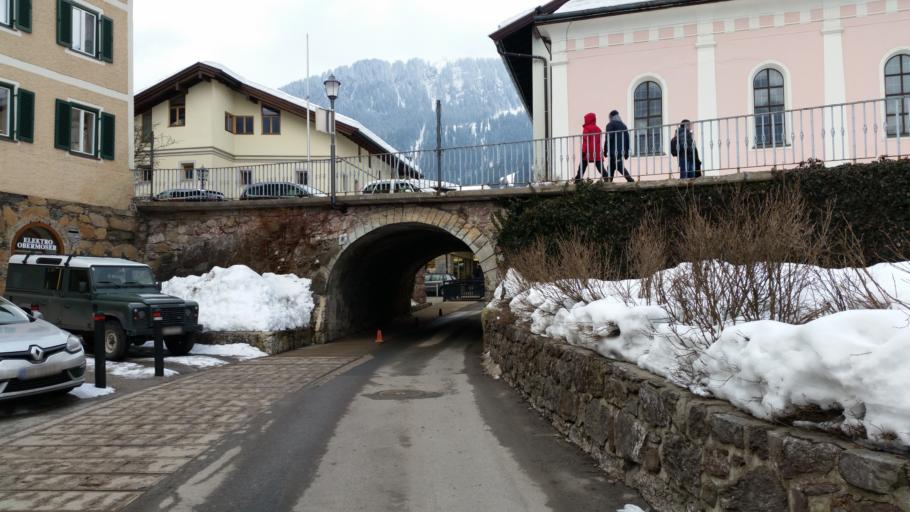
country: AT
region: Tyrol
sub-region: Politischer Bezirk Kitzbuhel
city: Kitzbuhel
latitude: 47.4479
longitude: 12.3900
